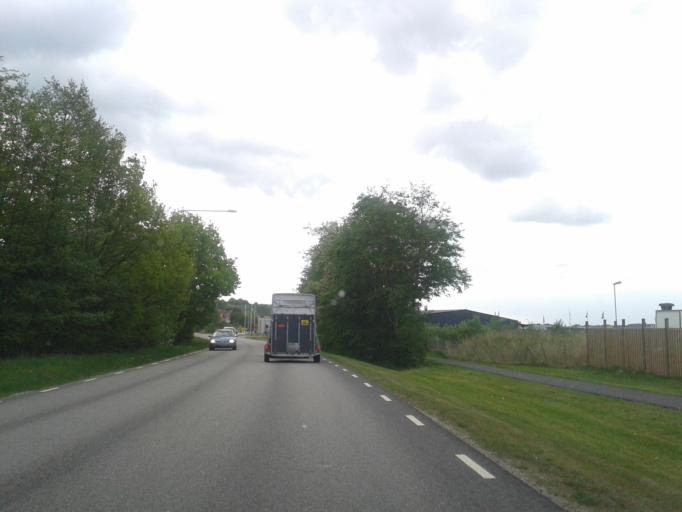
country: SE
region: Vaestra Goetaland
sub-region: Kungalvs Kommun
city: Kungalv
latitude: 57.8830
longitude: 11.9871
